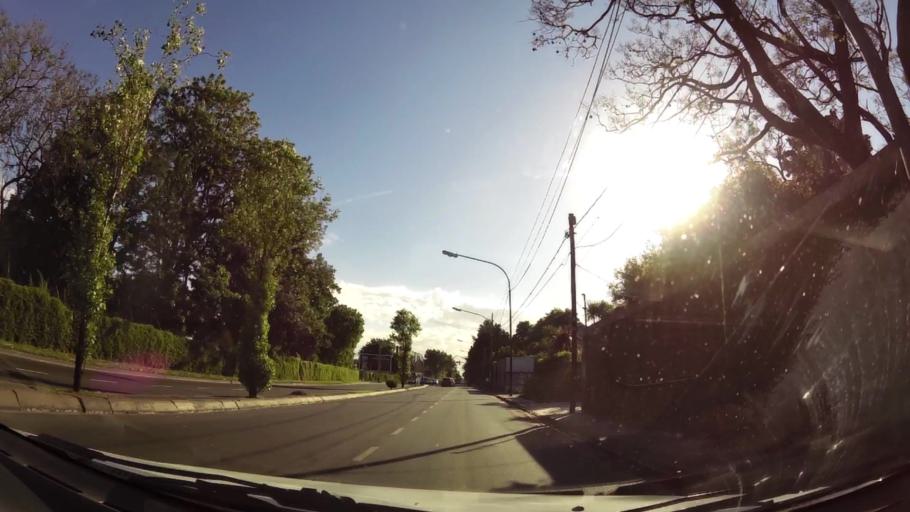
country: AR
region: Buenos Aires
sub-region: Partido de San Isidro
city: San Isidro
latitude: -34.4868
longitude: -58.5367
